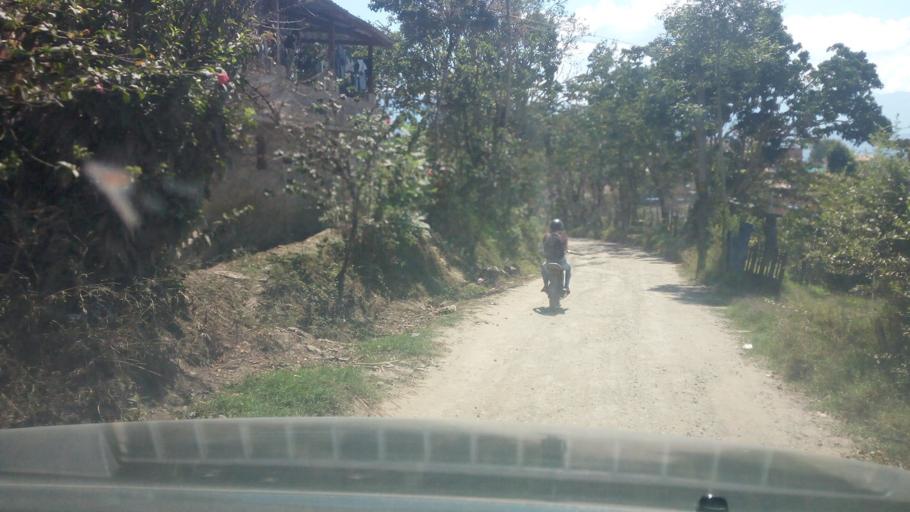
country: CO
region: Boyaca
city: Somondoco
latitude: 4.9862
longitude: -73.4296
